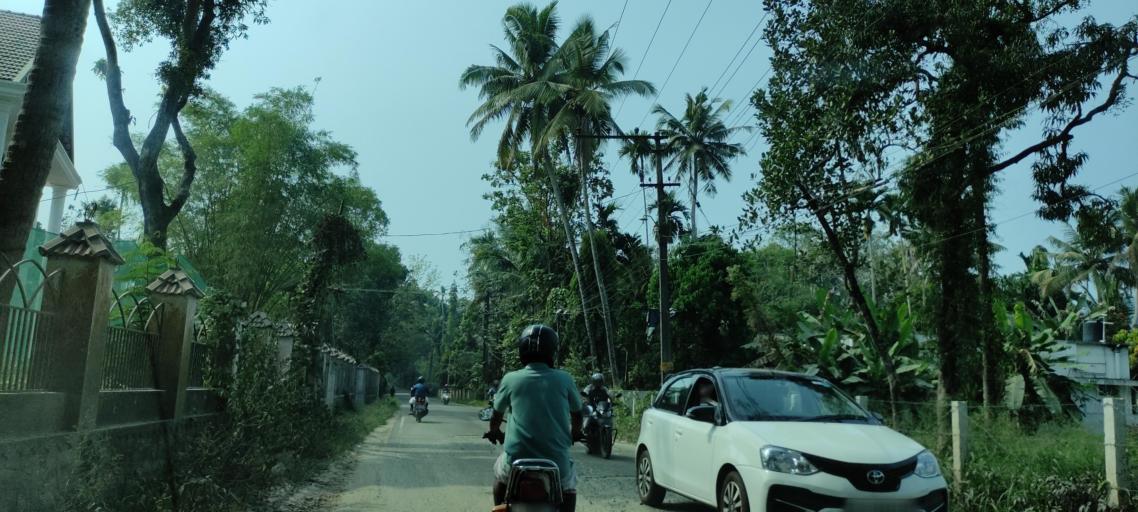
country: IN
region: Kerala
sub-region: Kottayam
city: Vaikam
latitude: 9.7383
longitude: 76.4129
